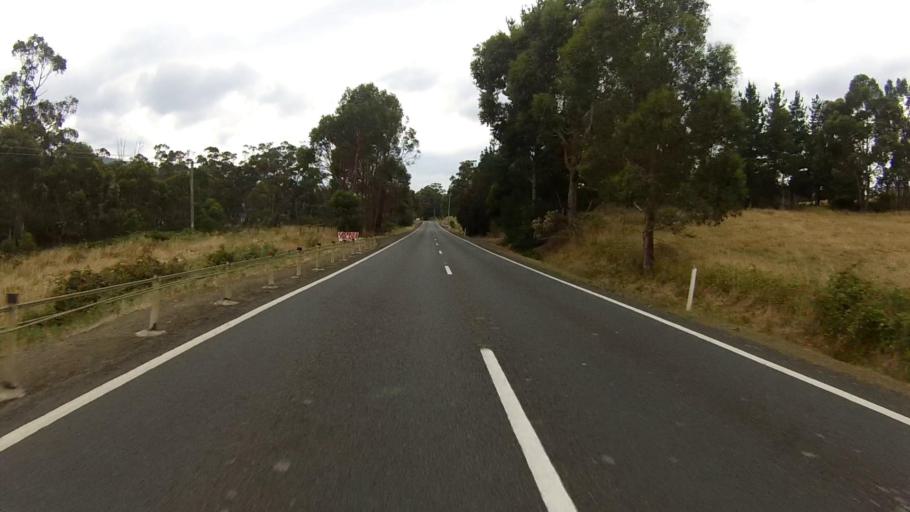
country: AU
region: Tasmania
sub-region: Huon Valley
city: Franklin
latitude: -43.0814
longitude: 147.0314
